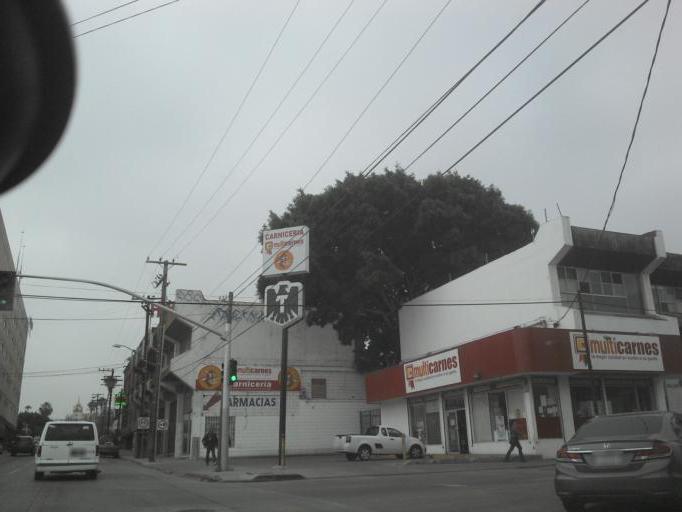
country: MX
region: Baja California
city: Tijuana
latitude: 32.5196
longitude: -117.0224
